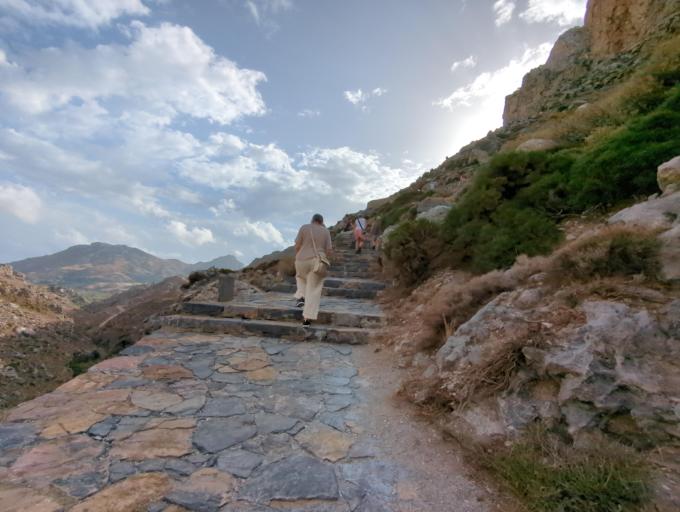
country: GR
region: Crete
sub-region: Nomos Rethymnis
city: Atsipopoulon
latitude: 35.1958
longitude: 24.4651
